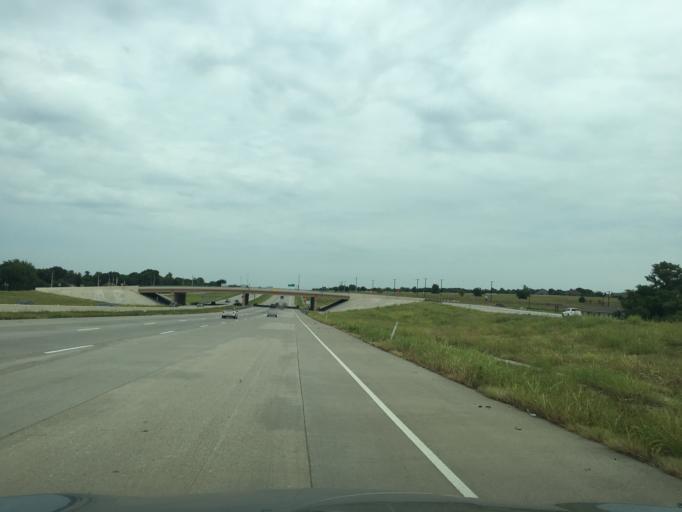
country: US
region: Texas
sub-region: Collin County
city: Melissa
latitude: 33.2826
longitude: -96.5923
